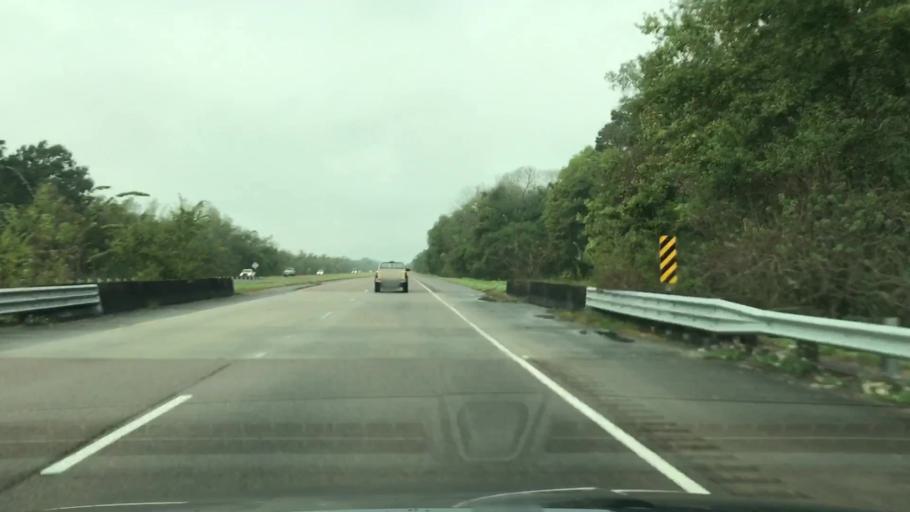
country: US
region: Louisiana
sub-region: Terrebonne Parish
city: Bayou Cane
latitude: 29.6871
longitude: -90.7036
